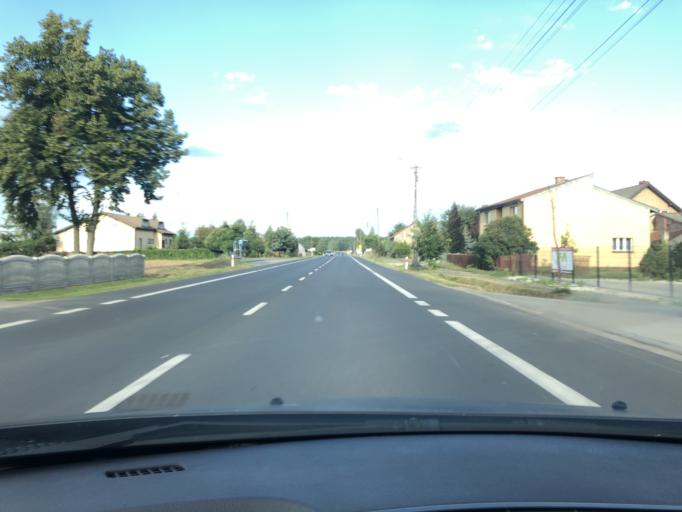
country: PL
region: Lodz Voivodeship
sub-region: Powiat wieruszowski
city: Galewice
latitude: 51.3041
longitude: 18.2431
